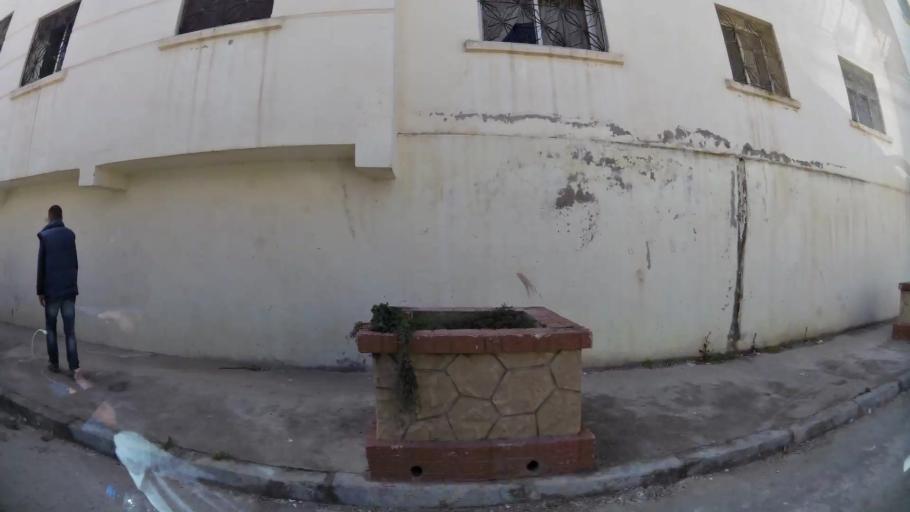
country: MA
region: Tanger-Tetouan
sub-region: Tanger-Assilah
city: Tangier
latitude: 35.7326
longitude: -5.8146
